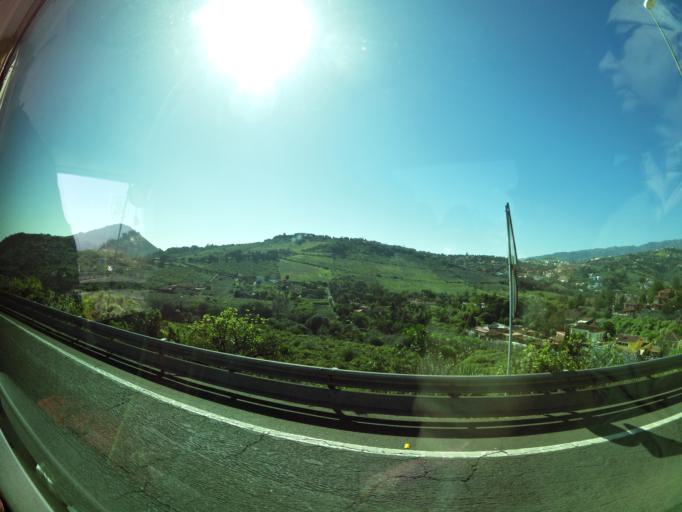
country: ES
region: Canary Islands
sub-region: Provincia de Las Palmas
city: Santa Brigida
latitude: 28.0460
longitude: -15.4732
